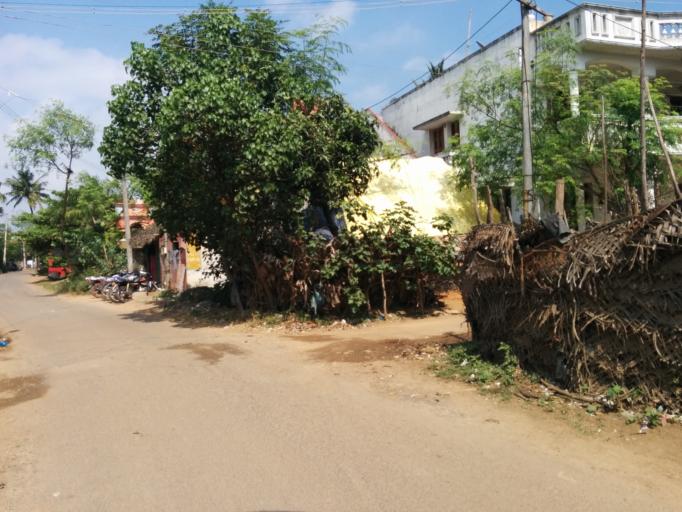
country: IN
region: Tamil Nadu
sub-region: Villupuram
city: Auroville
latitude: 11.9953
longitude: 79.8023
